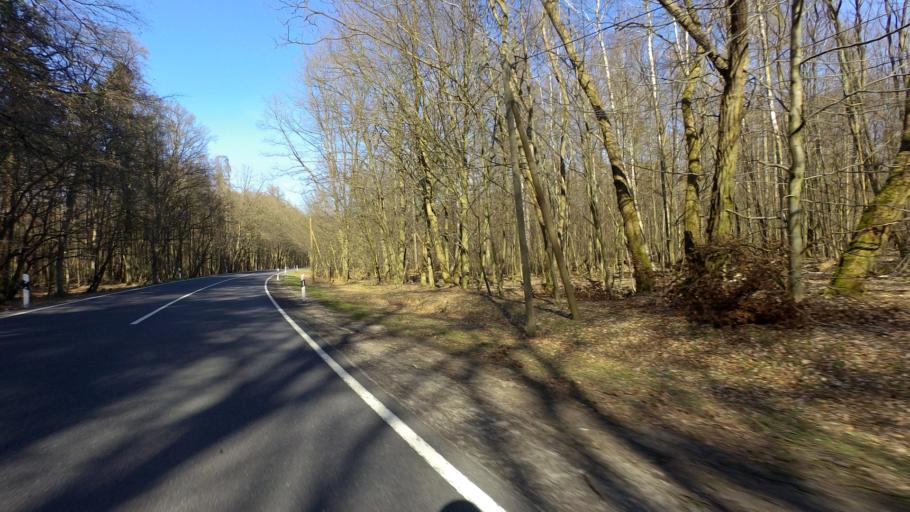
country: DE
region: Brandenburg
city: Chorin
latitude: 52.9127
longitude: 13.8964
